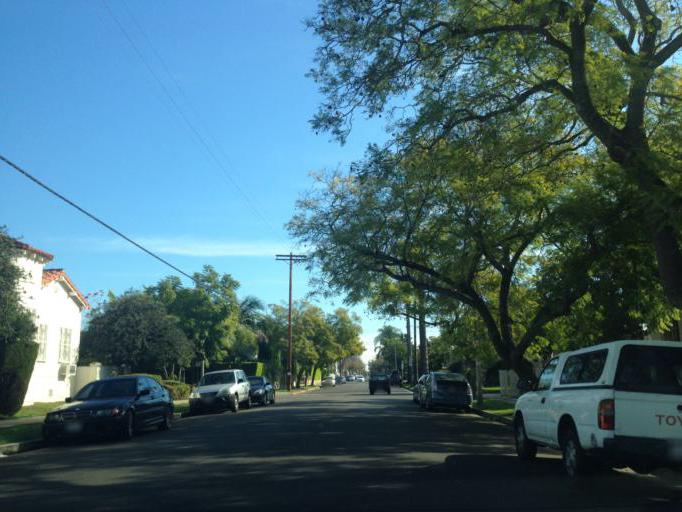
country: US
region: California
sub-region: Los Angeles County
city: West Hollywood
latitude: 34.0782
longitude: -118.3654
